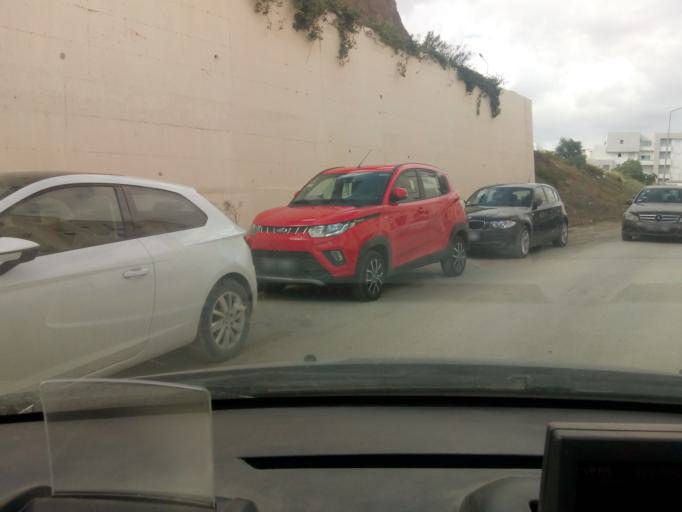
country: TN
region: Ariana
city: Ariana
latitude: 36.8762
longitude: 10.1789
